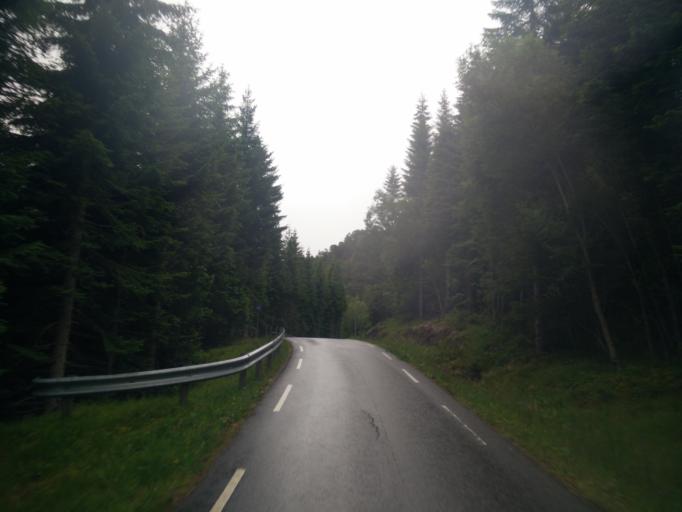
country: NO
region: More og Romsdal
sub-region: Kristiansund
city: Rensvik
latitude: 63.0308
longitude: 7.9107
